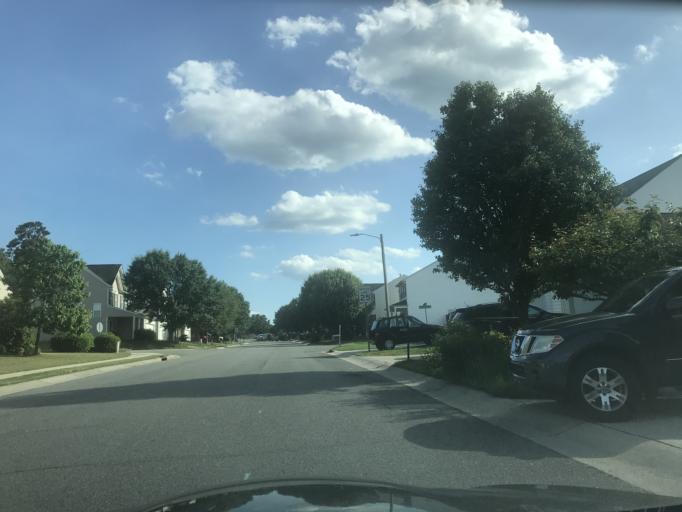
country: US
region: North Carolina
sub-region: Wake County
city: Knightdale
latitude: 35.8377
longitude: -78.5481
